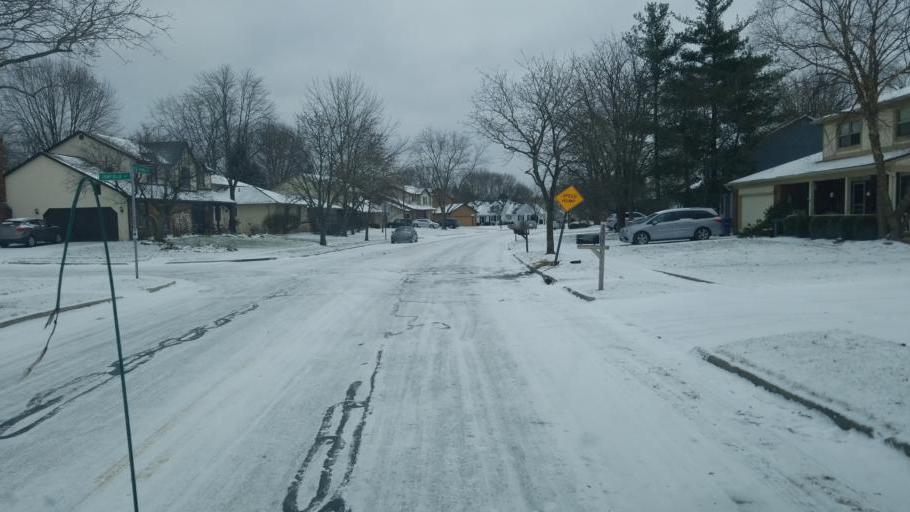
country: US
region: Ohio
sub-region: Delaware County
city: Powell
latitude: 40.1283
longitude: -83.0756
